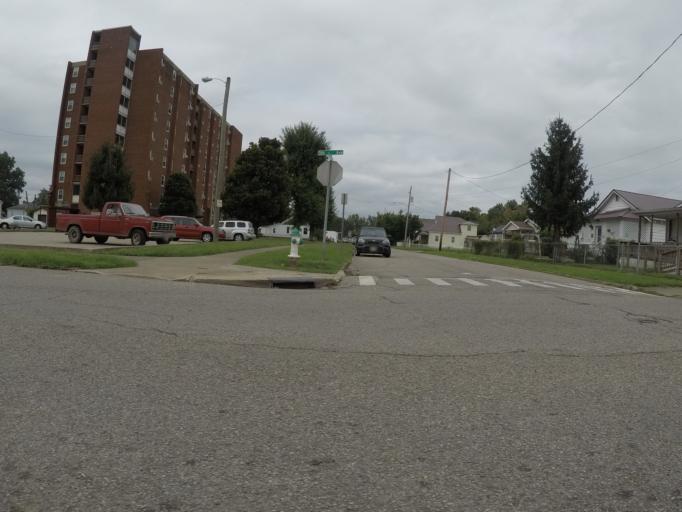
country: US
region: West Virginia
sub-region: Cabell County
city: Huntington
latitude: 38.4273
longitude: -82.3849
